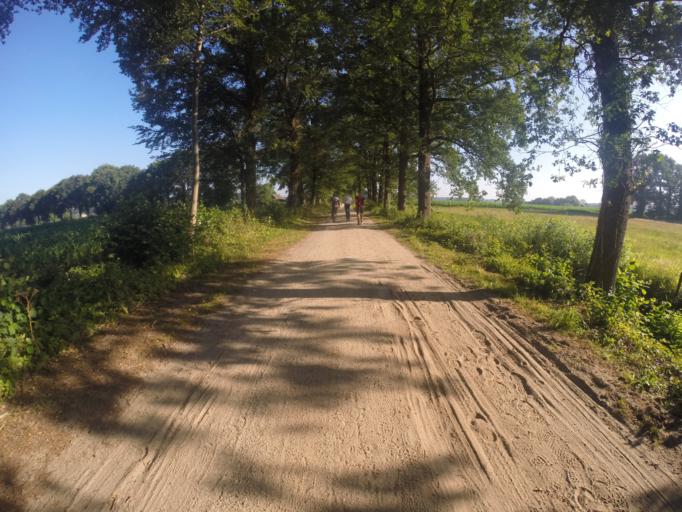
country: NL
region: Gelderland
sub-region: Gemeente Lochem
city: Lochem
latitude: 52.1141
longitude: 6.3717
